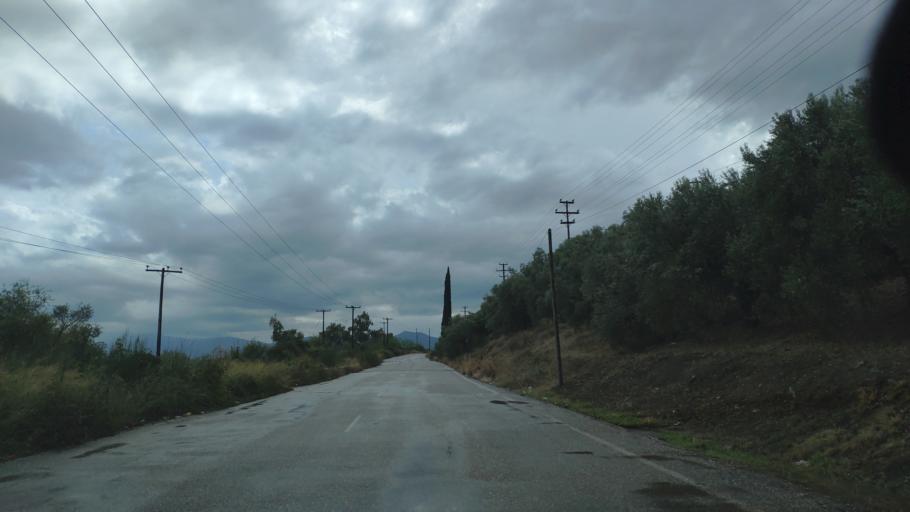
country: GR
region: West Greece
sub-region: Nomos Aitolias kai Akarnanias
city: Neapolis
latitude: 38.6727
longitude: 21.3246
